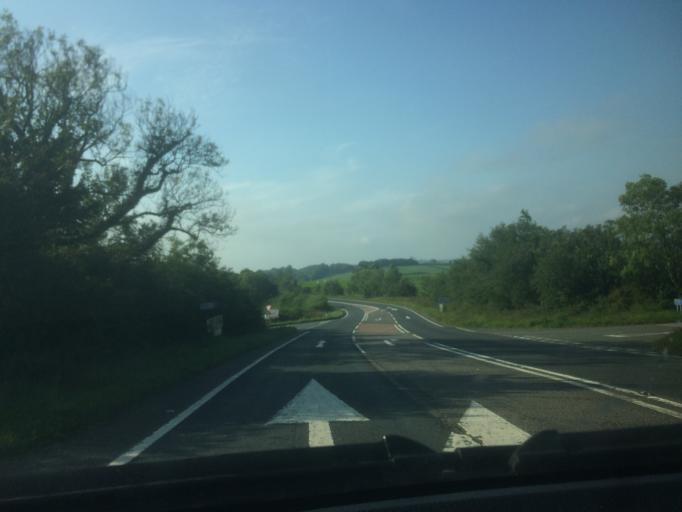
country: GB
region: England
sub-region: Cornwall
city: Pillaton
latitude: 50.4518
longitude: -4.2557
